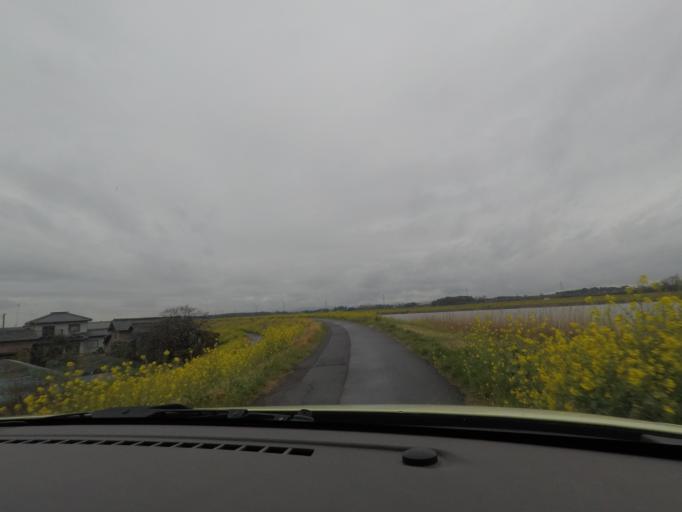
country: JP
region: Ibaraki
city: Mitsukaido
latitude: 36.0474
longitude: 140.0246
